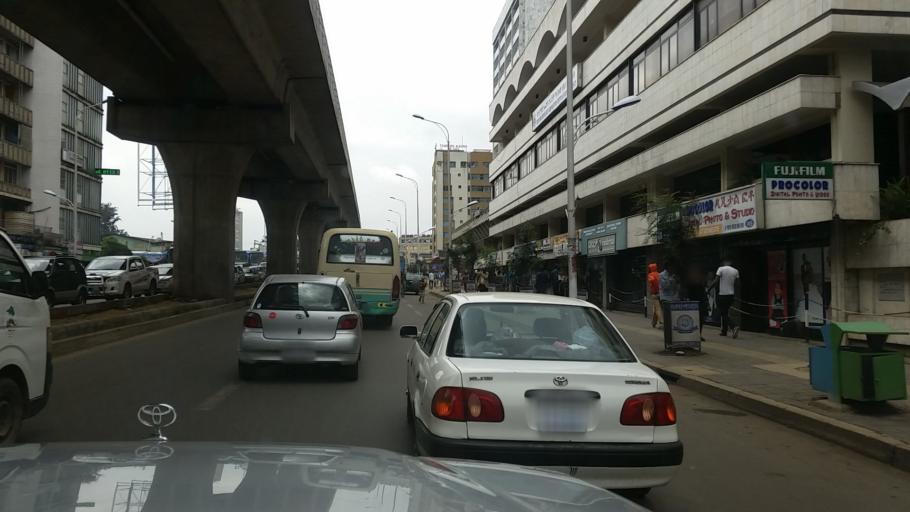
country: ET
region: Adis Abeba
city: Addis Ababa
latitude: 9.0119
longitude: 38.7526
